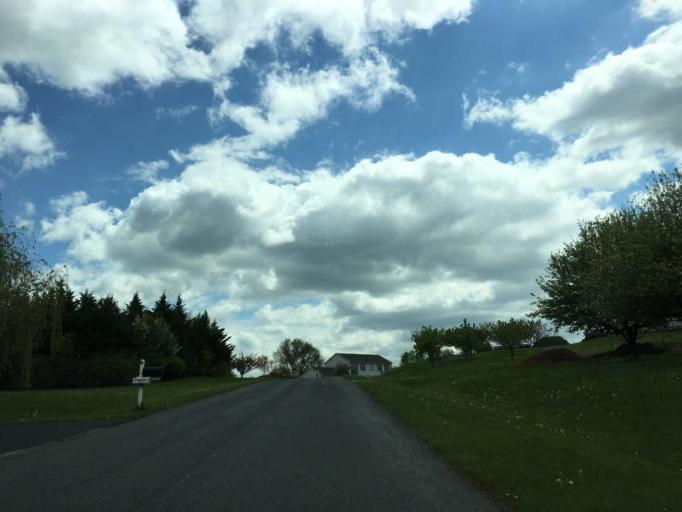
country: US
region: Maryland
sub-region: Frederick County
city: Thurmont
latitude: 39.6333
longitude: -77.3951
